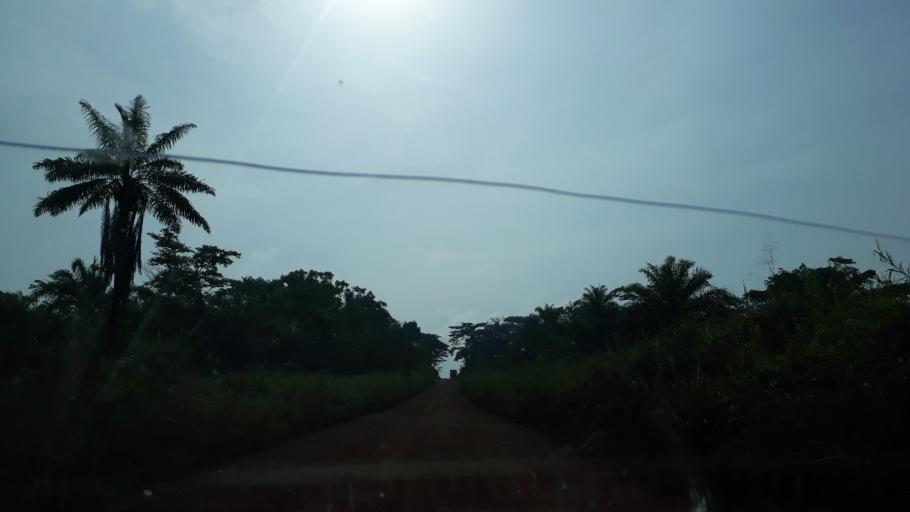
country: CD
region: Eastern Province
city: Wamba
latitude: 1.4083
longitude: 27.6363
